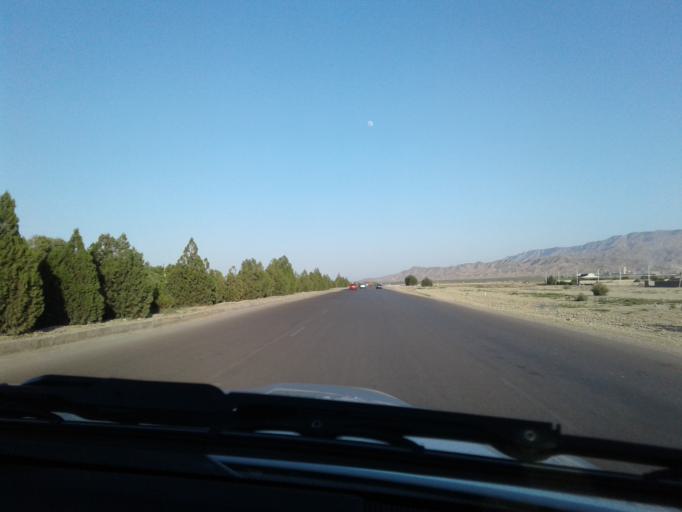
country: TM
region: Ahal
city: Baharly
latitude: 38.3062
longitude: 57.6212
